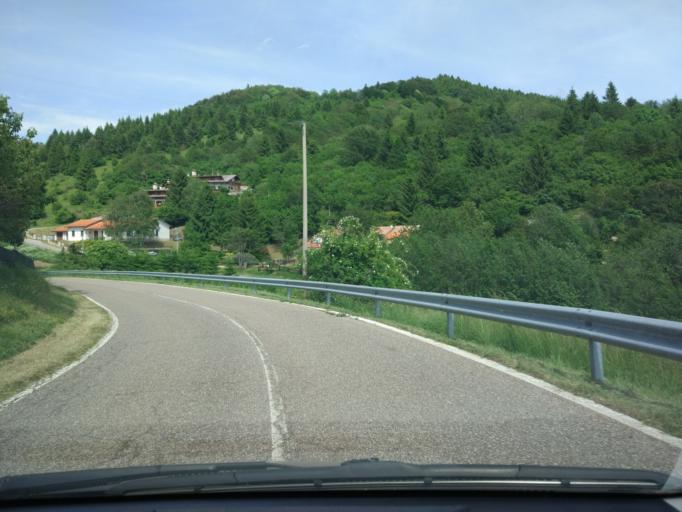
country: IT
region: Veneto
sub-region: Provincia di Verona
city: Ferrara di Monte Baldo
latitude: 45.6775
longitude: 10.8608
